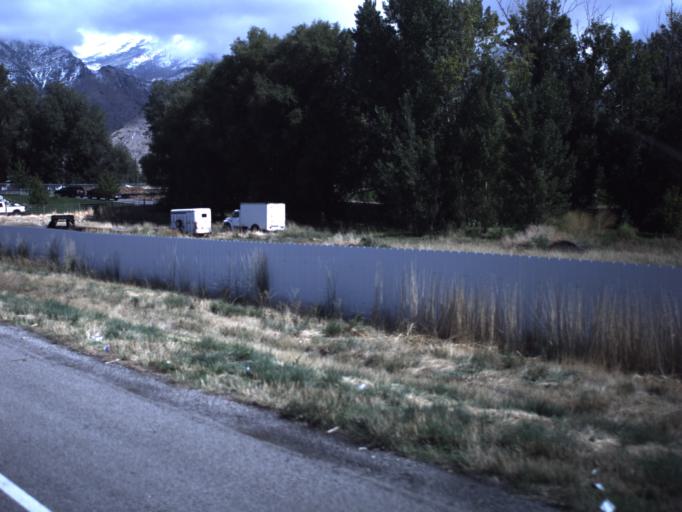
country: US
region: Utah
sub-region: Utah County
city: Springville
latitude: 40.1522
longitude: -111.6117
